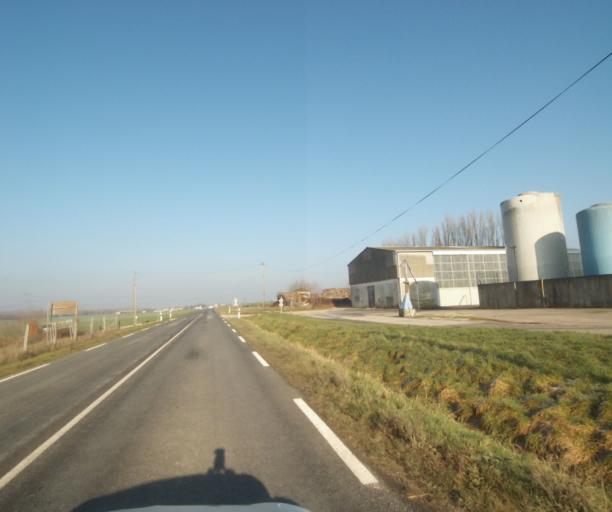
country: FR
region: Champagne-Ardenne
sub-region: Departement de la Haute-Marne
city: Wassy
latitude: 48.5129
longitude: 4.9371
